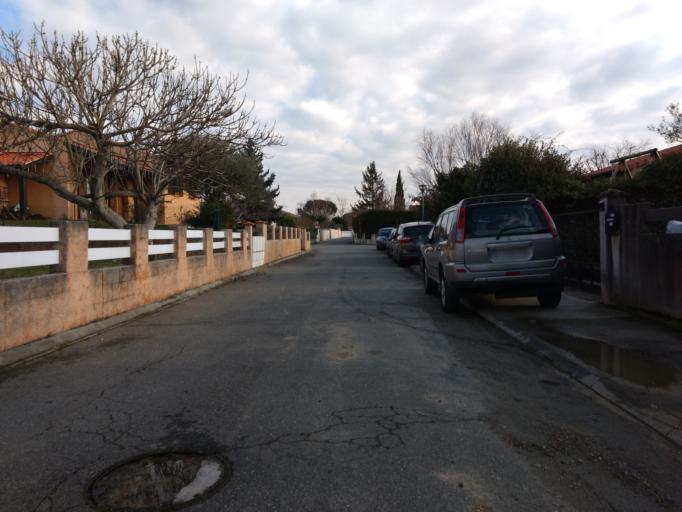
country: FR
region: Midi-Pyrenees
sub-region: Departement de la Haute-Garonne
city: Tournefeuille
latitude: 43.5811
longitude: 1.3546
